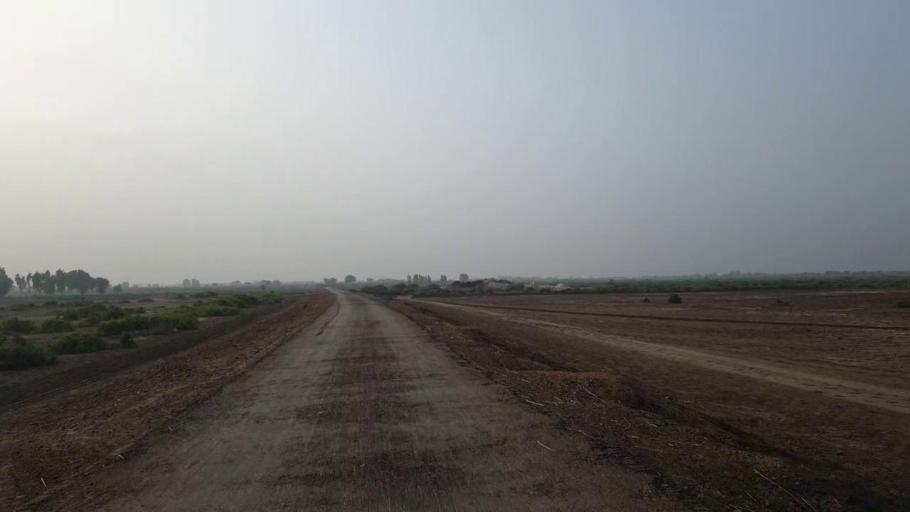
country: PK
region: Sindh
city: Tando Muhammad Khan
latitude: 25.1594
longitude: 68.6098
